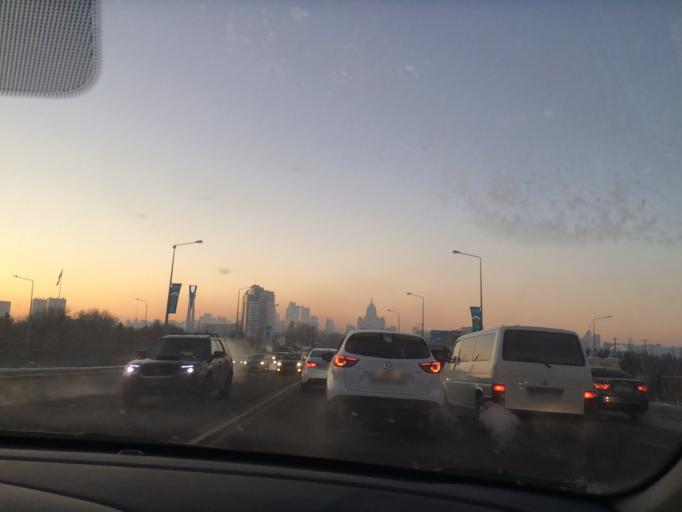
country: KZ
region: Astana Qalasy
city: Astana
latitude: 51.1563
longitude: 71.4115
